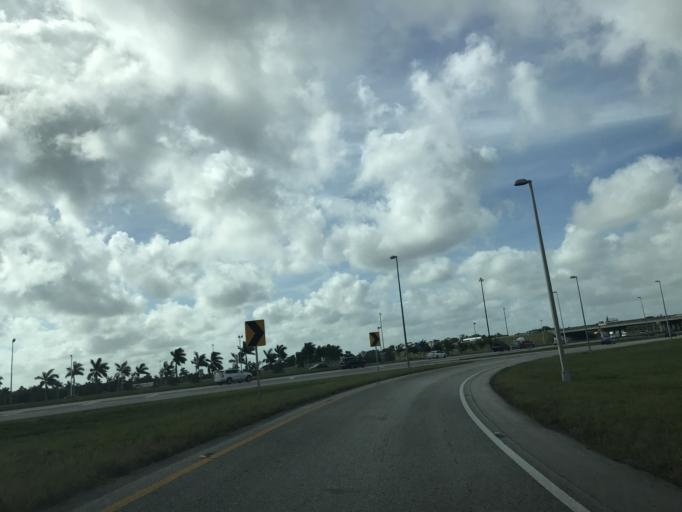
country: US
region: Florida
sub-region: Palm Beach County
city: Boca Pointe
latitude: 26.3063
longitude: -80.1665
